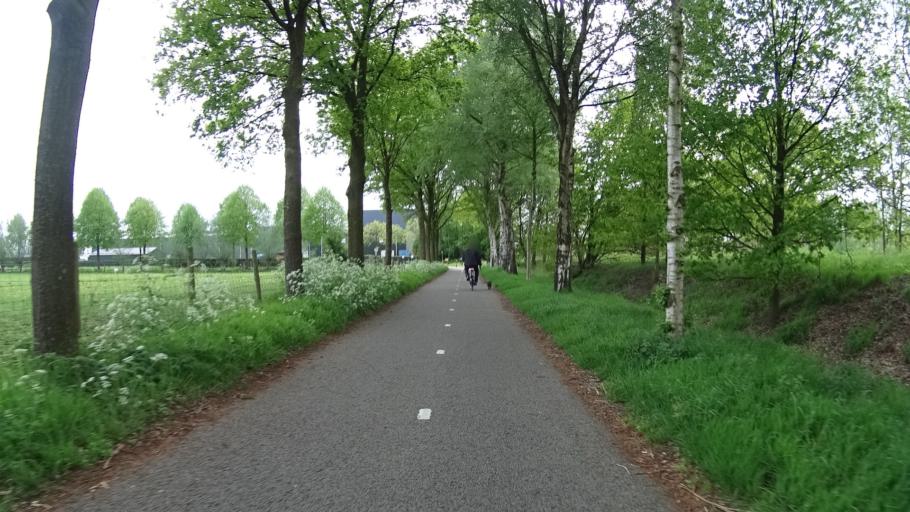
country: NL
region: North Brabant
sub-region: Gemeente Veghel
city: Veghel
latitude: 51.6213
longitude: 5.5300
